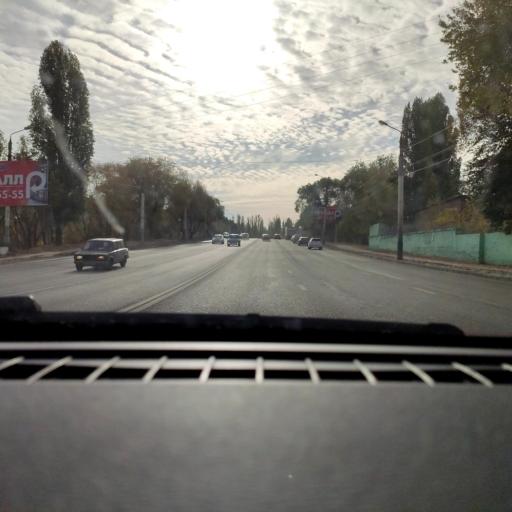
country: RU
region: Voronezj
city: Voronezh
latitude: 51.6238
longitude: 39.2334
